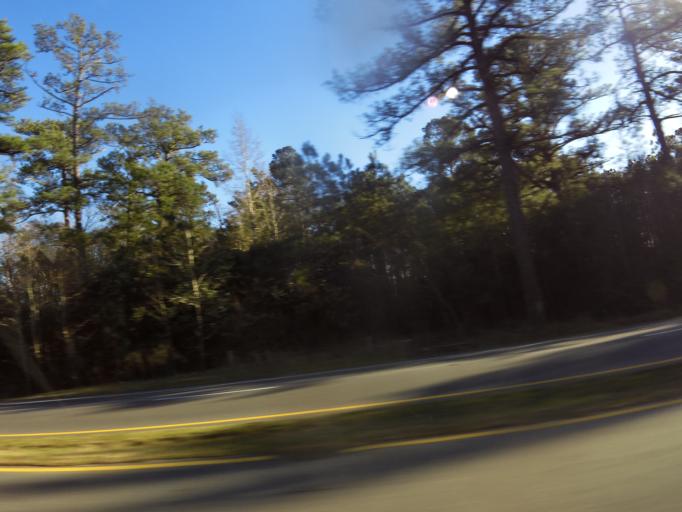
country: US
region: Virginia
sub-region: City of Suffolk
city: South Suffolk
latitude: 36.7028
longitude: -76.6950
